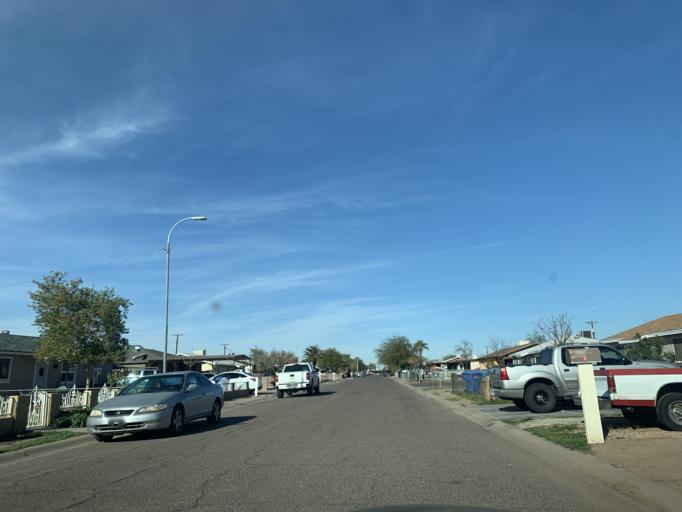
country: US
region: Arizona
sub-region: Maricopa County
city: Laveen
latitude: 33.4002
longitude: -112.1365
